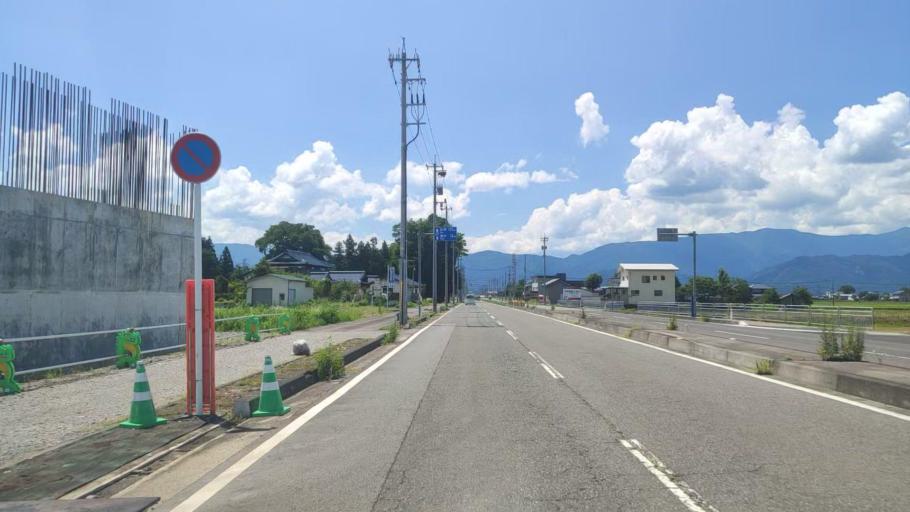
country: JP
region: Fukui
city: Ono
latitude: 35.9979
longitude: 136.5092
